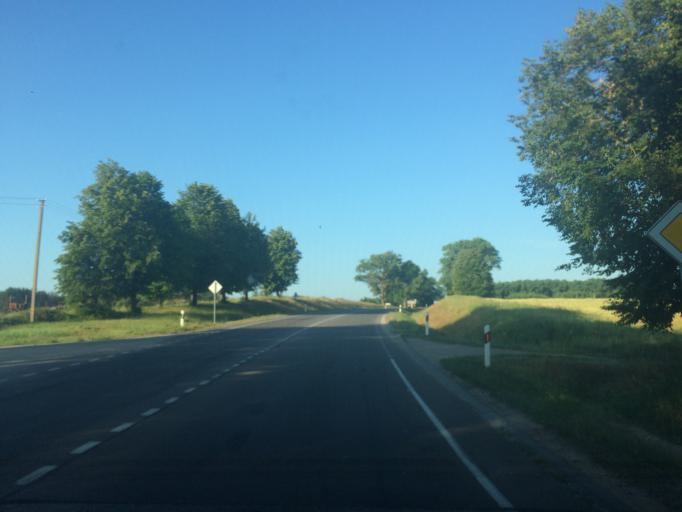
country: LT
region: Vilnius County
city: Ukmerge
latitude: 55.3023
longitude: 24.8600
